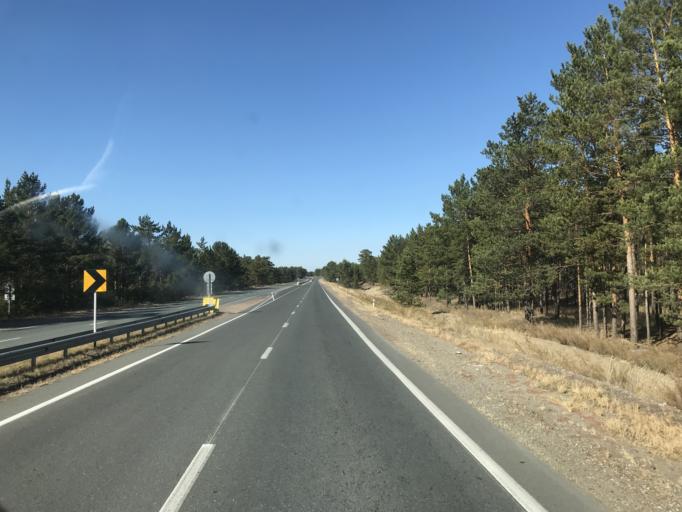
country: KZ
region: East Kazakhstan
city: Semey
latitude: 50.5002
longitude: 80.1174
